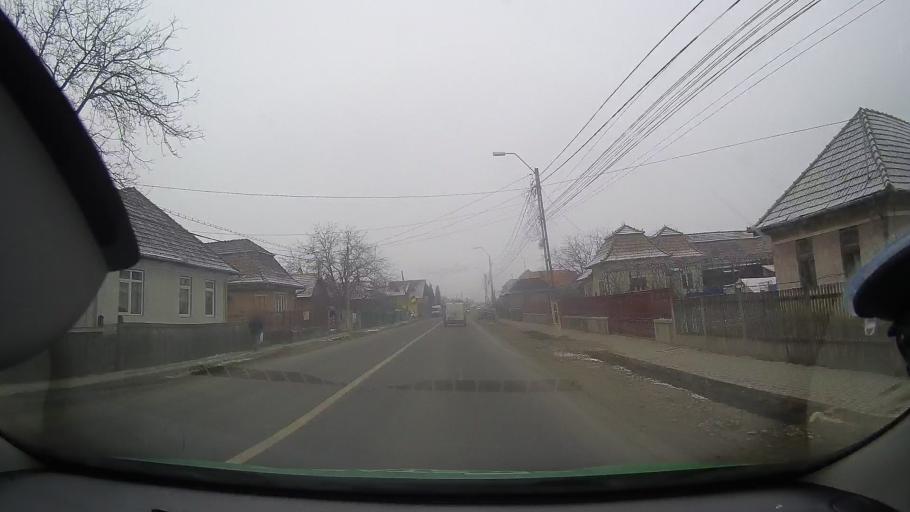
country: RO
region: Cluj
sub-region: Comuna Mihai Viteazu
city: Mihai Viteazu
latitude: 46.5384
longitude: 23.7361
